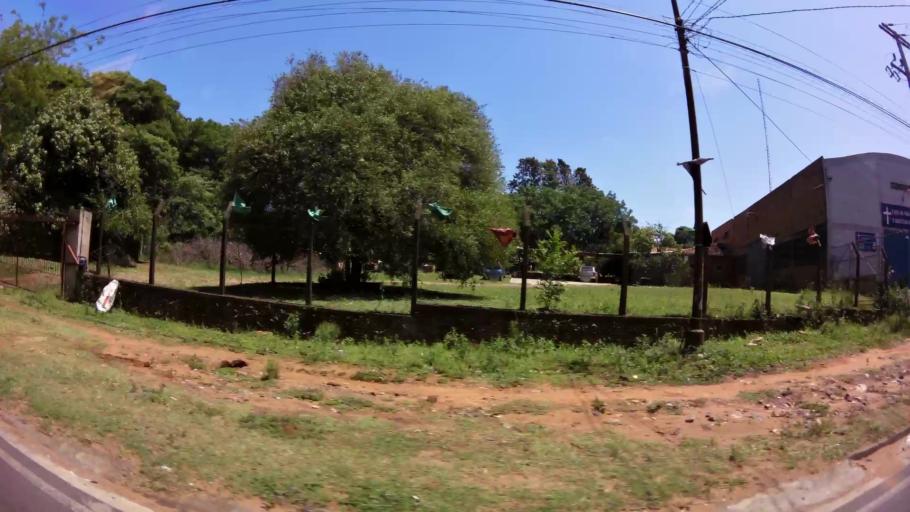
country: PY
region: Central
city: Nemby
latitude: -25.3837
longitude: -57.5221
